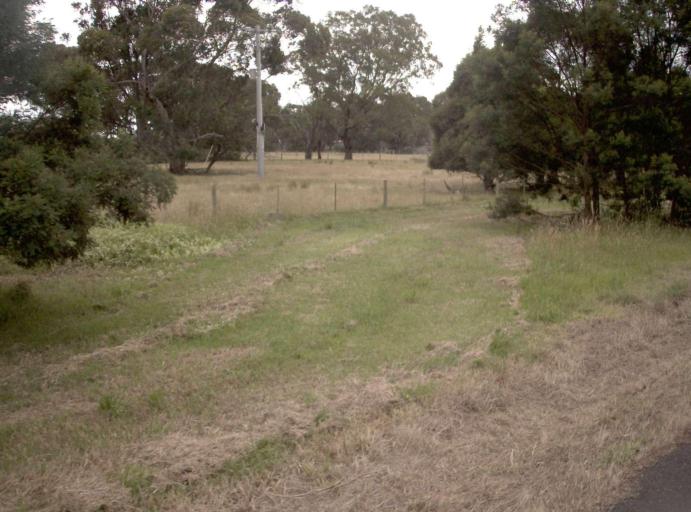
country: AU
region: Victoria
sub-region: Wellington
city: Sale
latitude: -38.3762
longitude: 146.9834
